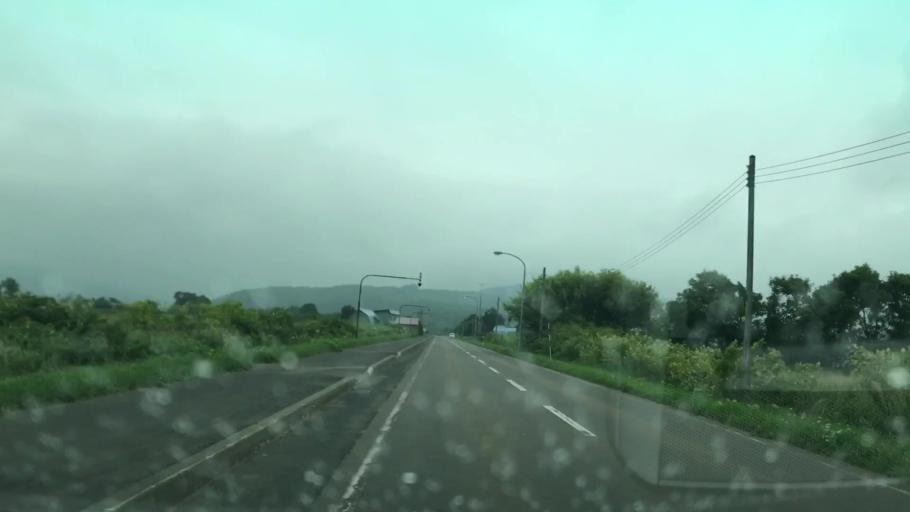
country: JP
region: Hokkaido
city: Iwanai
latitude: 42.7562
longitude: 140.2775
